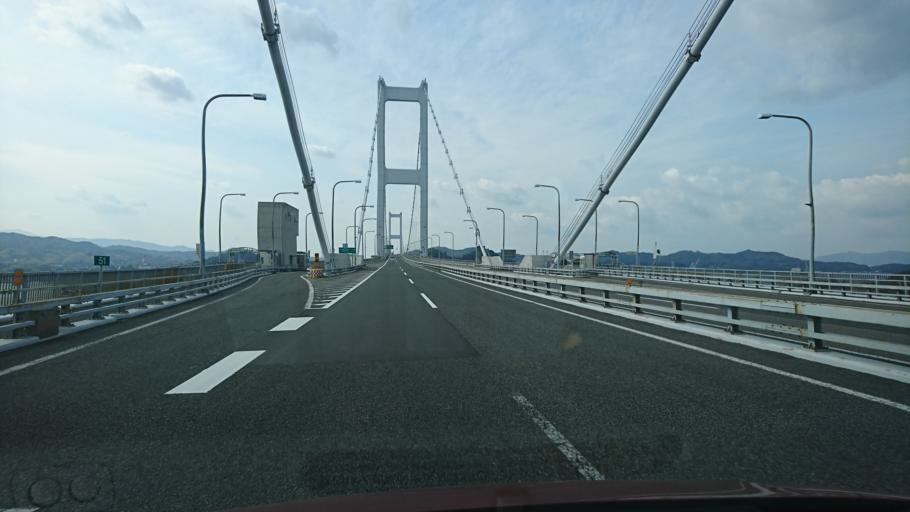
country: JP
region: Hiroshima
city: Takehara
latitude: 34.1185
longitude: 132.9933
